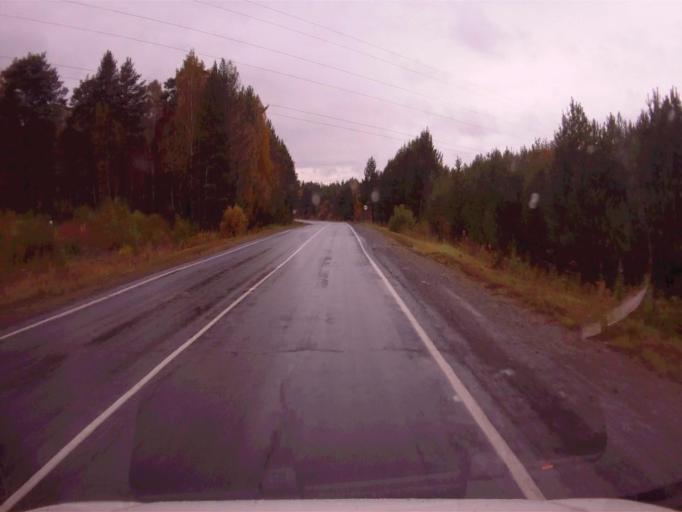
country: RU
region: Chelyabinsk
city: Verkhniy Ufaley
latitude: 56.0102
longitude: 60.3214
